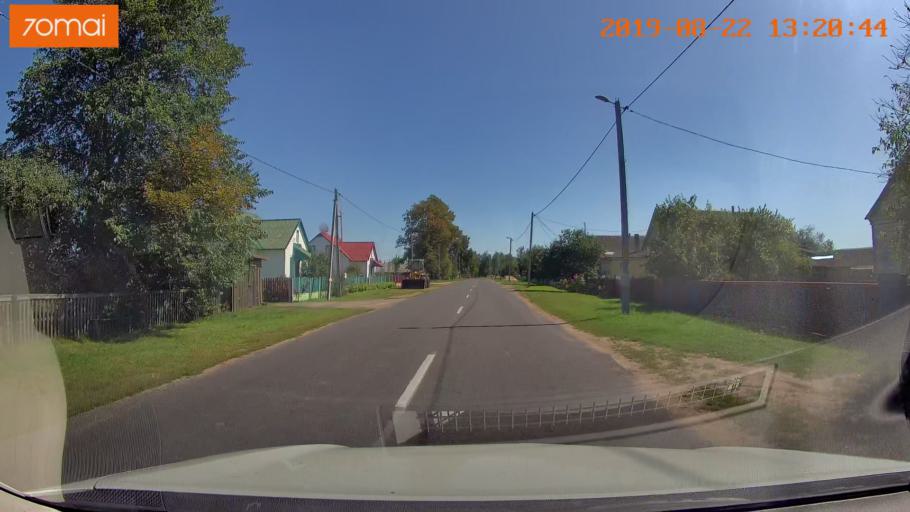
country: BY
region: Minsk
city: Urechcha
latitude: 53.2283
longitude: 27.9720
